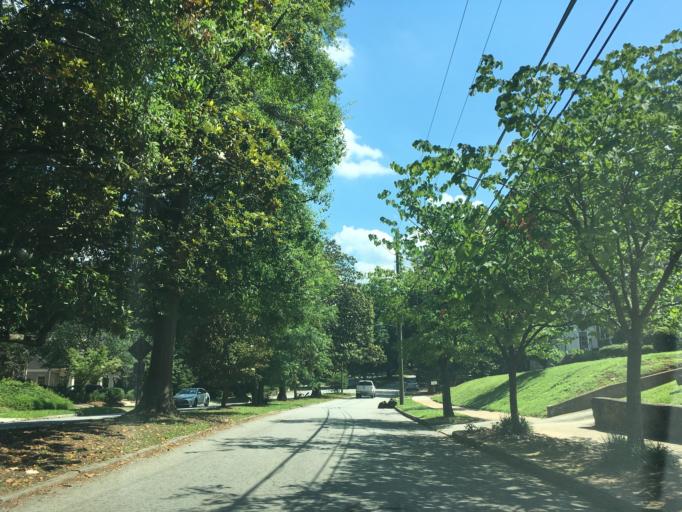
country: US
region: Georgia
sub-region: DeKalb County
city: Druid Hills
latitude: 33.7869
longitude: -84.3499
